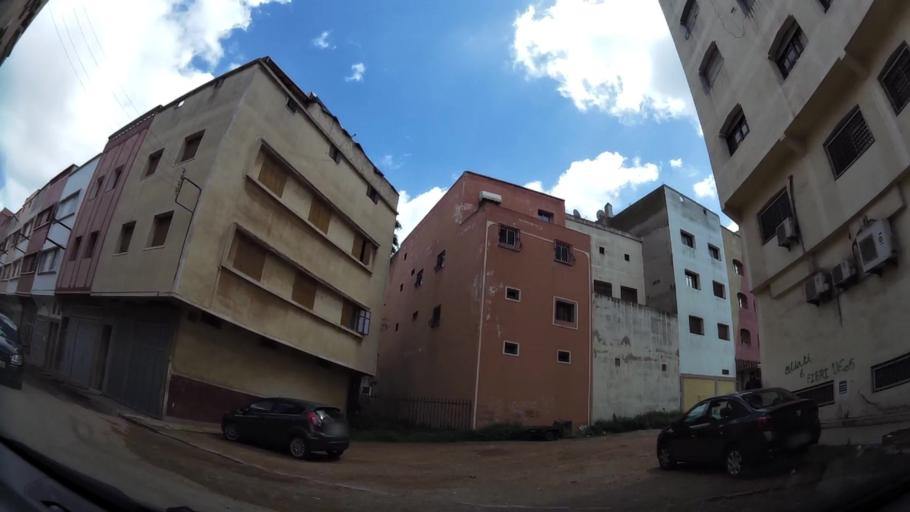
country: MA
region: Grand Casablanca
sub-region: Casablanca
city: Casablanca
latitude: 33.5374
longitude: -7.5875
